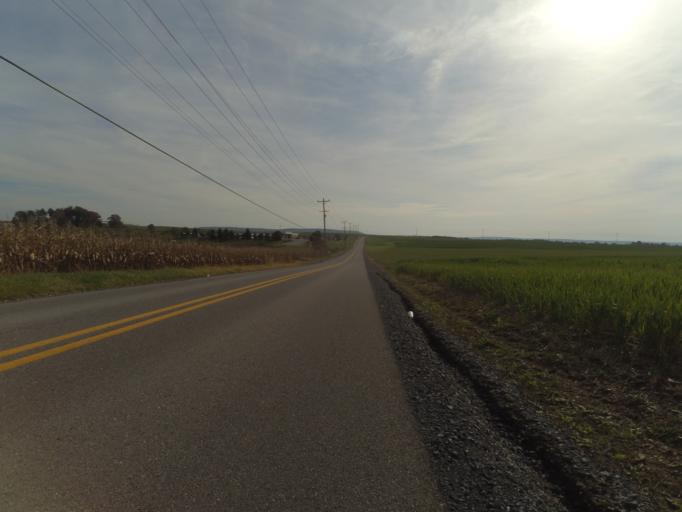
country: US
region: Pennsylvania
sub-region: Centre County
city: Houserville
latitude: 40.8491
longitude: -77.8633
